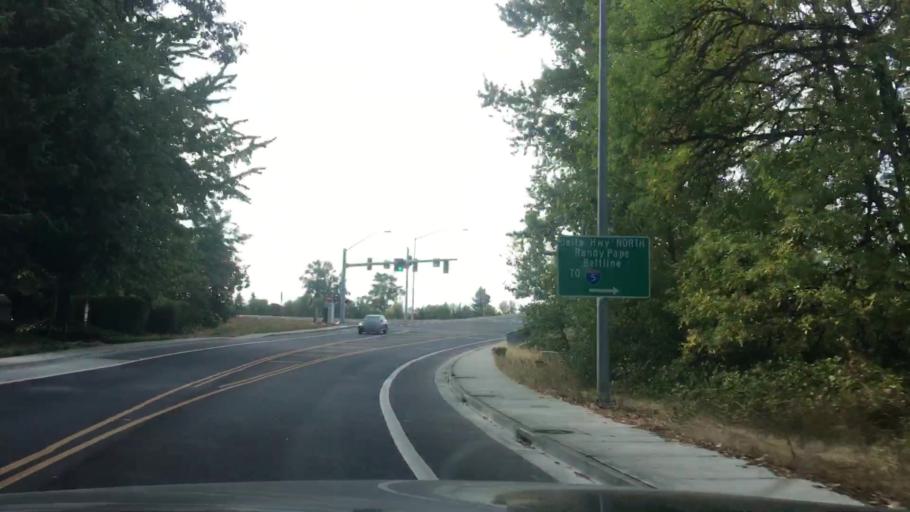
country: US
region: Oregon
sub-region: Lane County
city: Eugene
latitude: 44.0842
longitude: -123.1000
